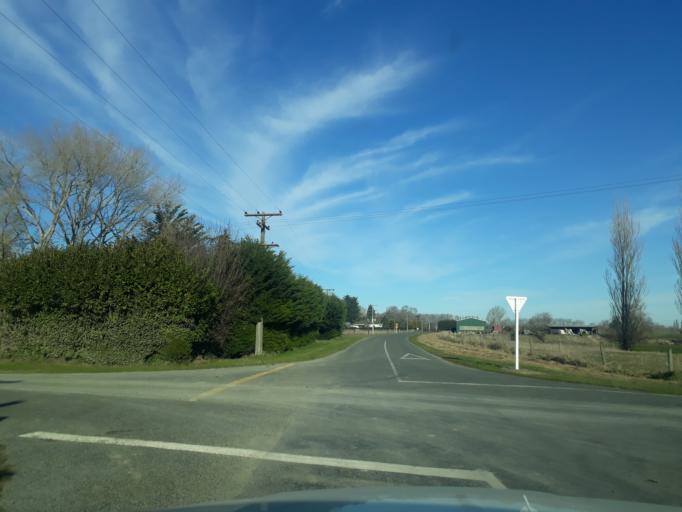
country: NZ
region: Canterbury
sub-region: Timaru District
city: Timaru
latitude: -44.2602
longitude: 171.3380
